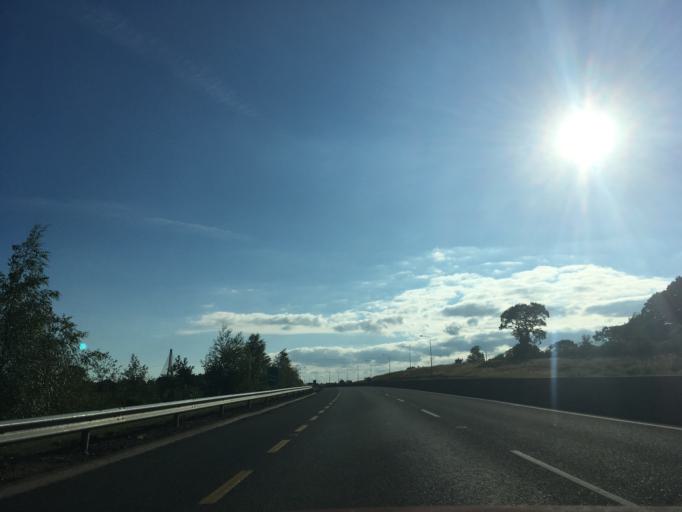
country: IE
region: Munster
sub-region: Waterford
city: Waterford
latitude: 52.2865
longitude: -7.1360
